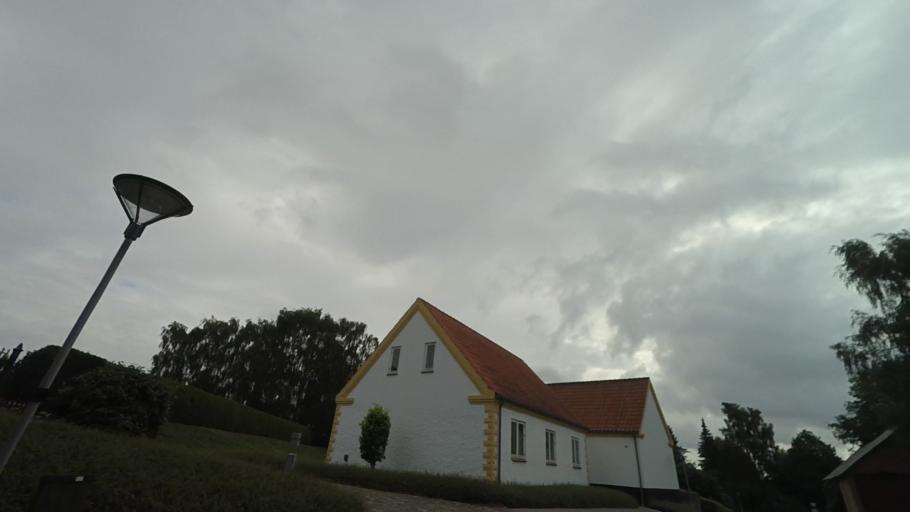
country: DK
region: Central Jutland
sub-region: Syddjurs Kommune
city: Ronde
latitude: 56.3420
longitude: 10.4606
